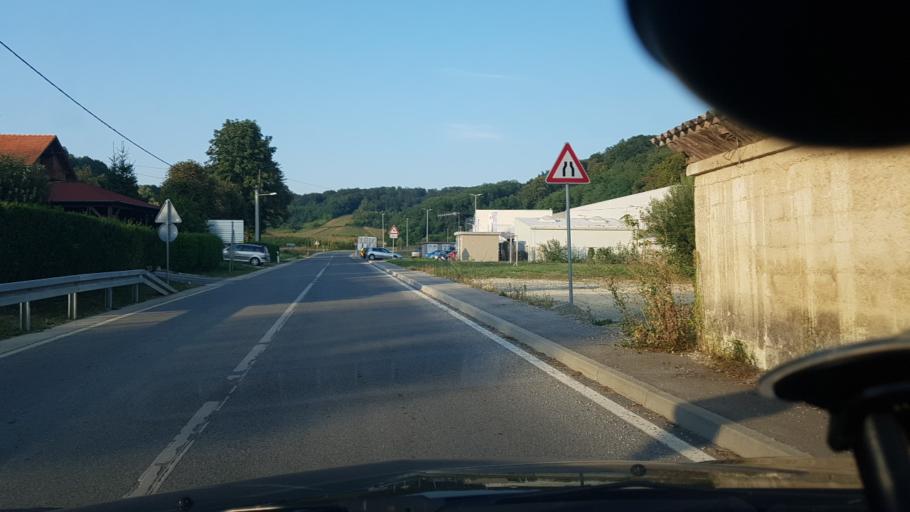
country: HR
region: Krapinsko-Zagorska
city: Pregrada
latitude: 46.1429
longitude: 15.7897
